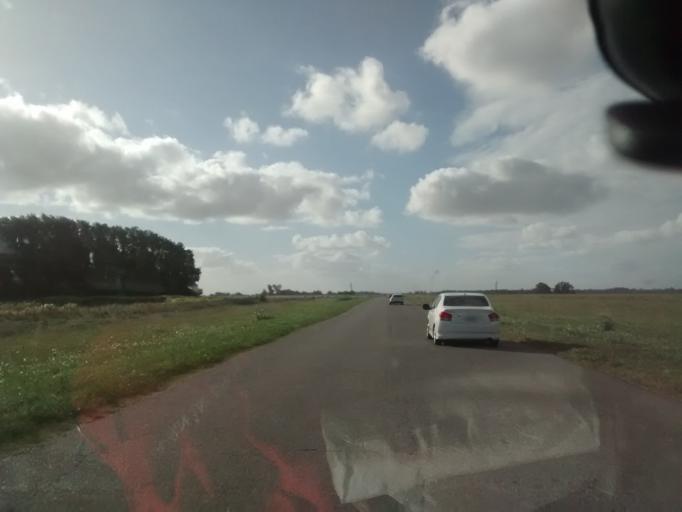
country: AR
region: Buenos Aires
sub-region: Partido de Ayacucho
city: Ayacucho
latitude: -37.2017
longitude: -58.5061
